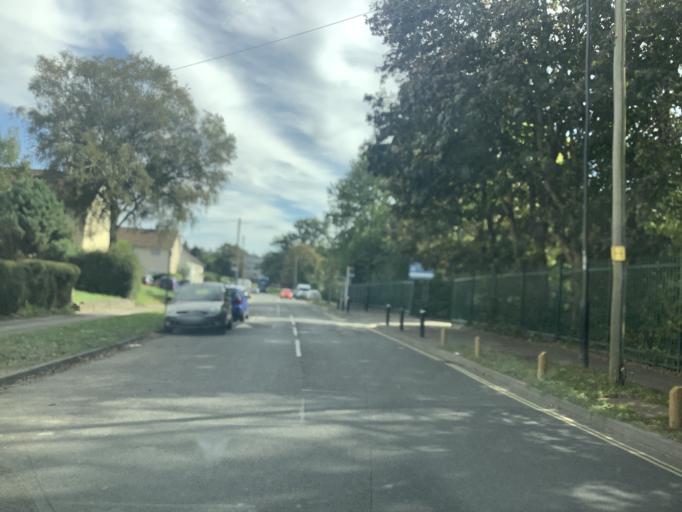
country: GB
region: England
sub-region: Hampshire
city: Totton
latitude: 50.9279
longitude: -1.4547
